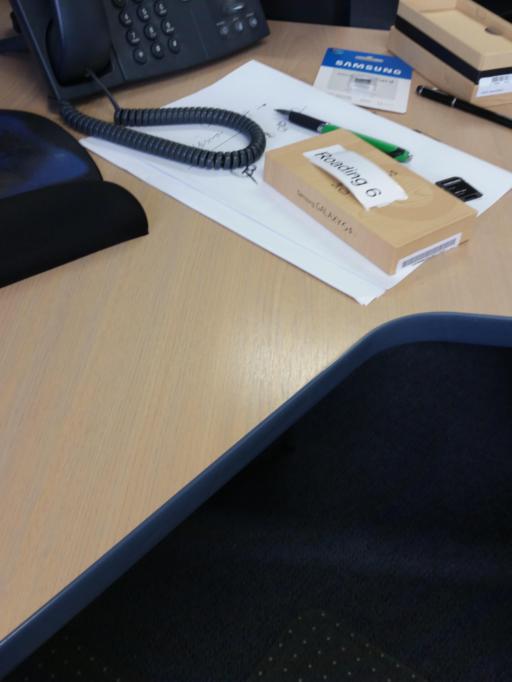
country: NZ
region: Southland
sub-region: Invercargill City
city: Invercargill
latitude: -46.4147
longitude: 168.3466
